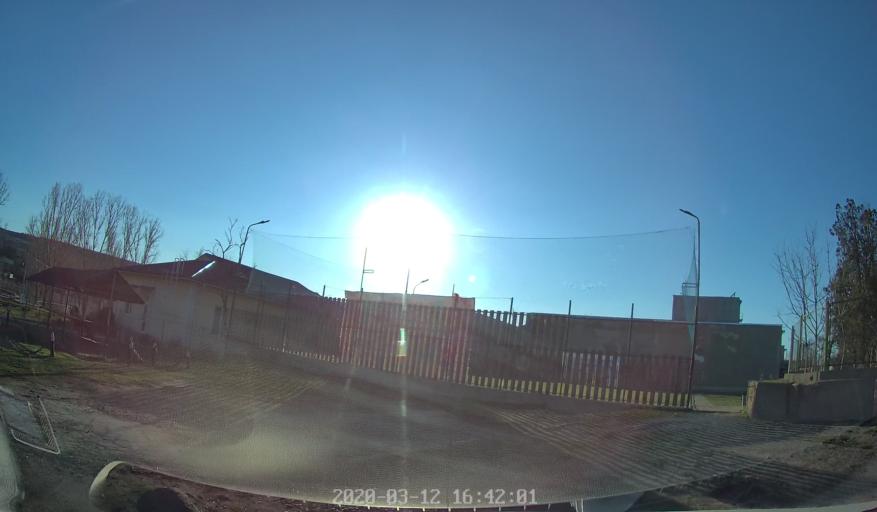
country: MD
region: Anenii Noi
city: Anenii Noi
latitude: 46.8217
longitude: 29.1381
